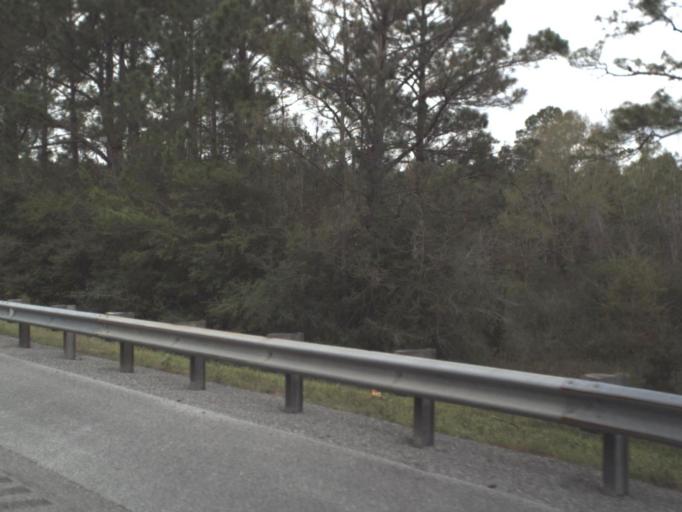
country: US
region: Florida
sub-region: Okaloosa County
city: Crestview
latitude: 30.7236
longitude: -86.4821
